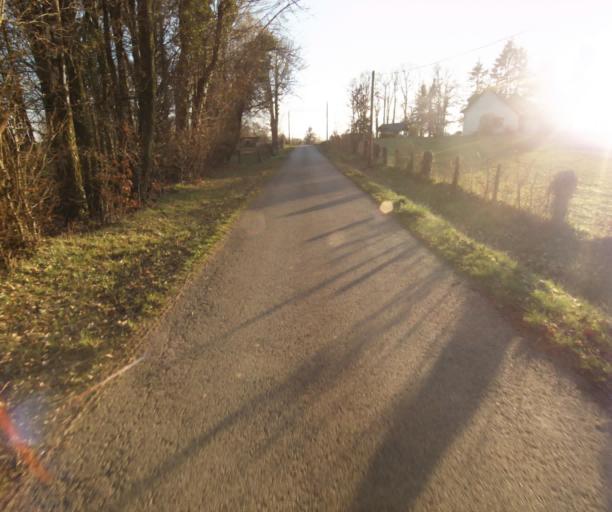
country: FR
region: Limousin
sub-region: Departement de la Correze
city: Uzerche
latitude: 45.3594
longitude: 1.5957
